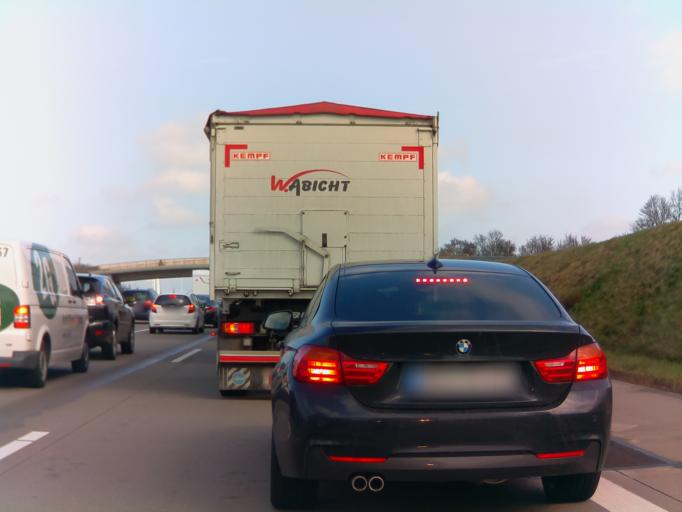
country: DE
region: Saxony-Anhalt
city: Brehna
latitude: 51.5980
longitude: 12.1833
